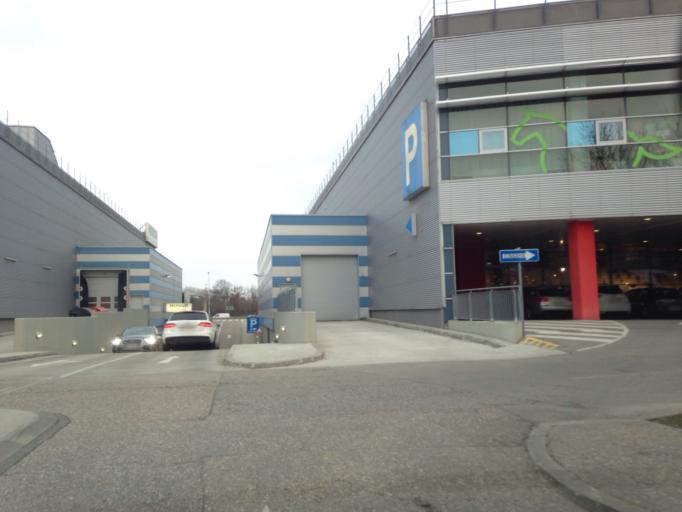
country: AT
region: Lower Austria
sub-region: Politischer Bezirk Wien-Umgebung
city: Gerasdorf bei Wien
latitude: 48.2502
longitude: 16.4678
